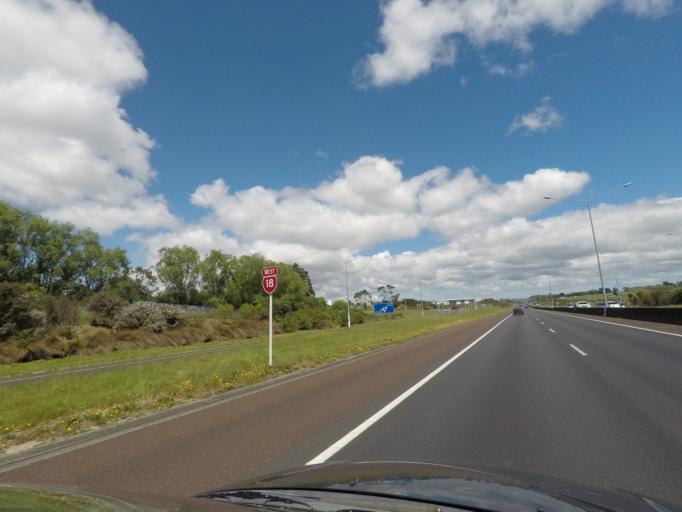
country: NZ
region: Auckland
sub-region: Auckland
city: Rosebank
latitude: -36.7982
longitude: 174.6415
